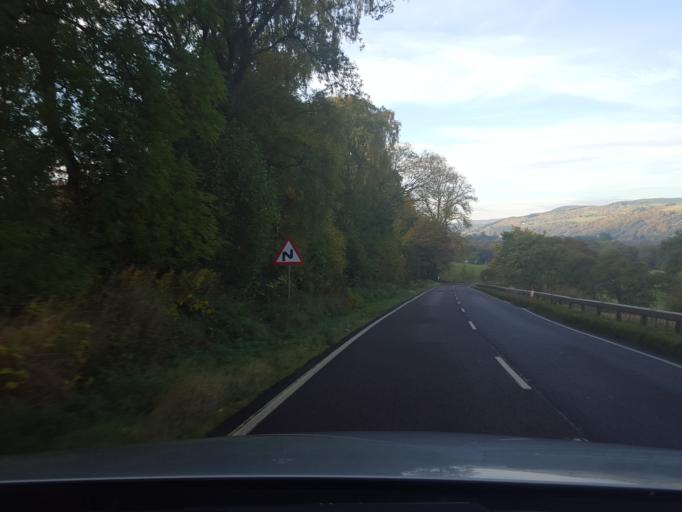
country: GB
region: Scotland
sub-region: Highland
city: Beauly
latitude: 57.3278
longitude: -4.4576
